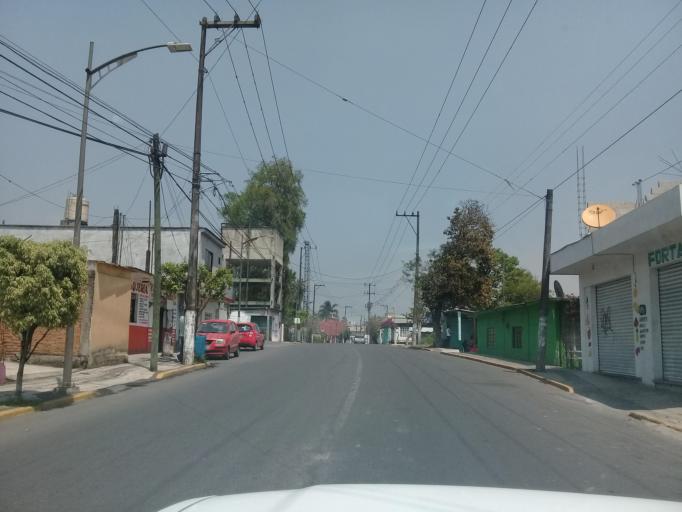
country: MX
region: Veracruz
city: Ixtac Zoquitlan
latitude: 18.8654
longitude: -97.0621
